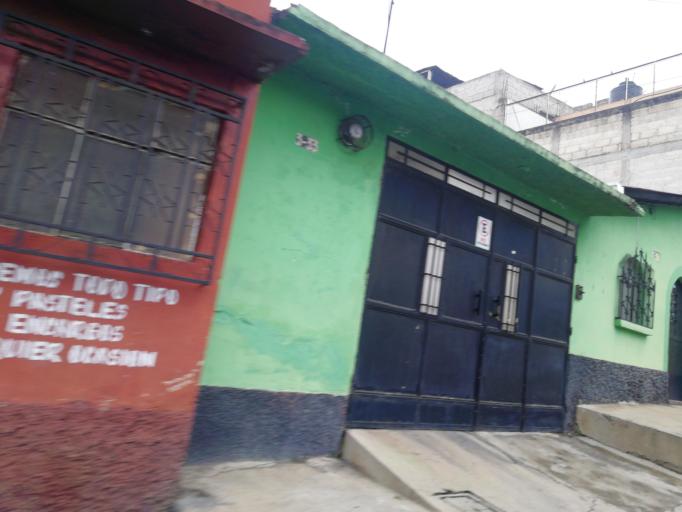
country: GT
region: Quetzaltenango
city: Quetzaltenango
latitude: 14.8524
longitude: -91.5152
